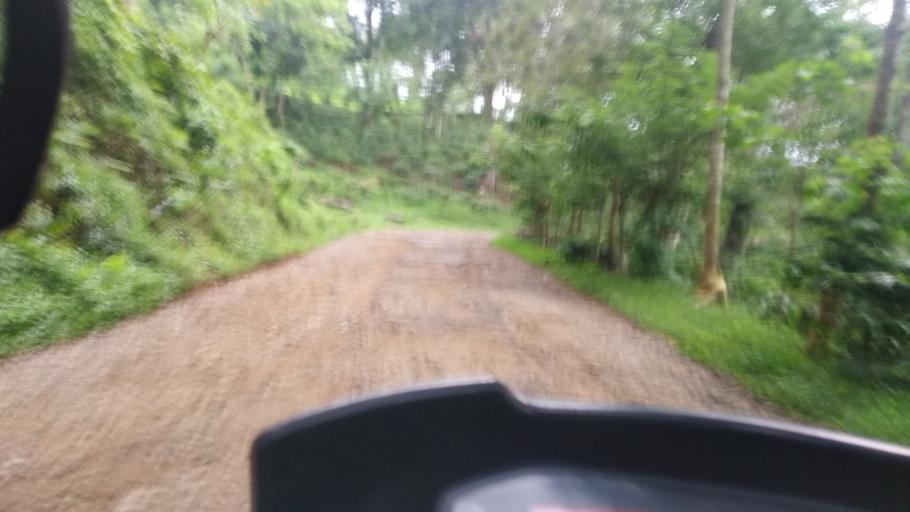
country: IN
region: Tamil Nadu
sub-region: Theni
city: Gudalur
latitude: 9.5546
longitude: 77.0648
